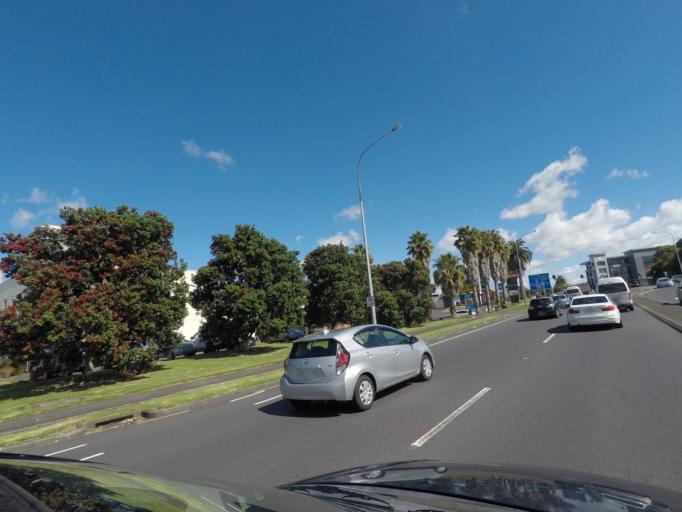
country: NZ
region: Auckland
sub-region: Auckland
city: Manukau City
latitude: -36.9893
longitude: 174.8830
